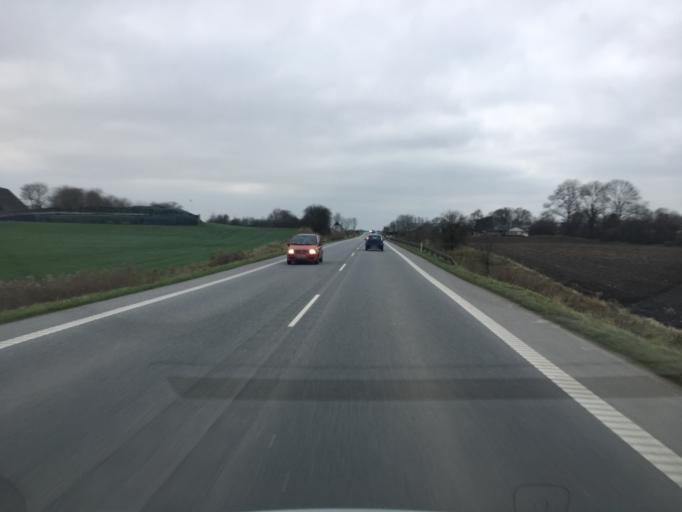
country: DK
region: South Denmark
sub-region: Aabenraa Kommune
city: Rodekro
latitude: 55.0259
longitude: 9.3520
